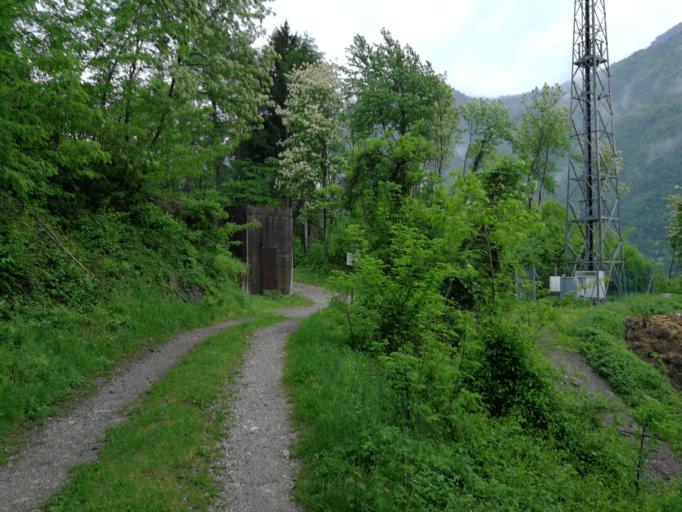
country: IT
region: Trentino-Alto Adige
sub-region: Provincia di Trento
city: Condino
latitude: 45.8815
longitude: 10.5896
